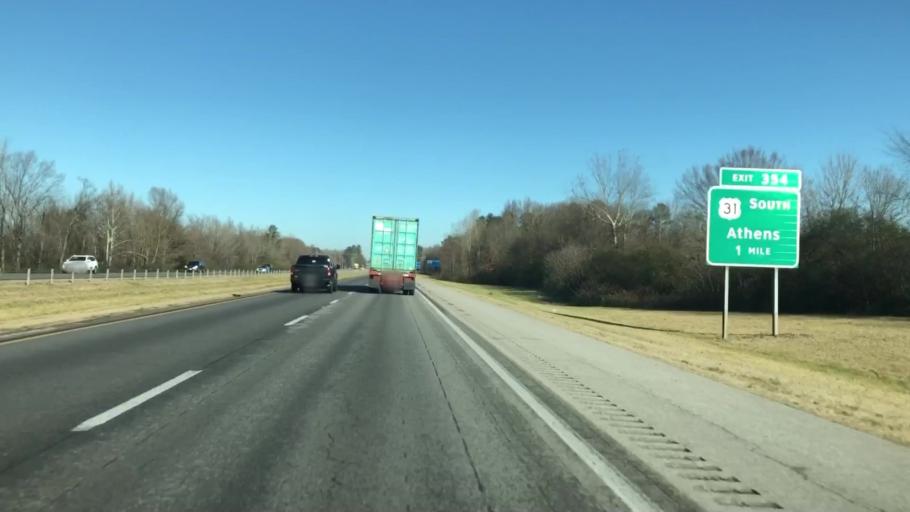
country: US
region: Alabama
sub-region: Limestone County
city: Athens
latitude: 34.8163
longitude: -86.9387
